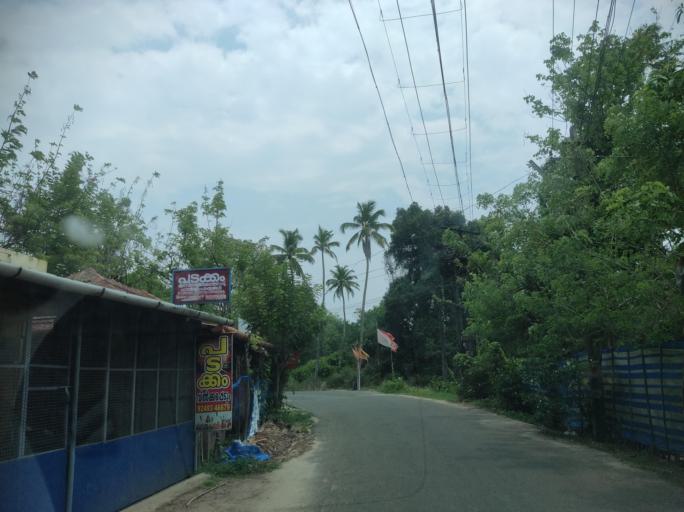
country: IN
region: Kerala
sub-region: Alappuzha
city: Kutiatodu
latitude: 9.7514
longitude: 76.3264
